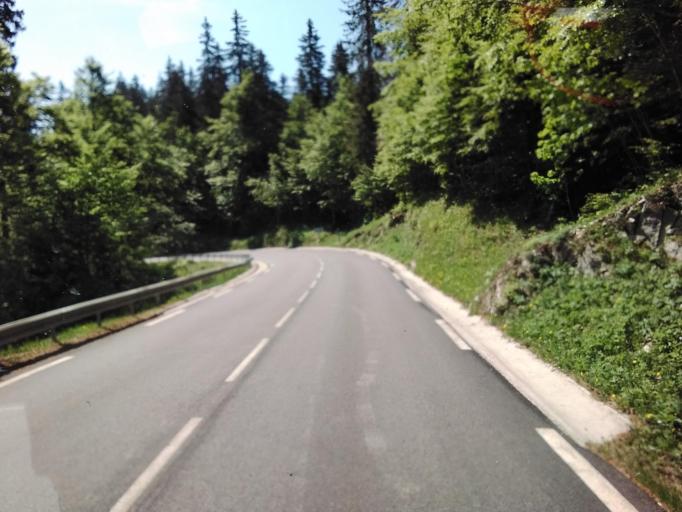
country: FR
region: Rhone-Alpes
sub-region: Departement de l'Ain
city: Gex
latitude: 46.3670
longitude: 6.0226
